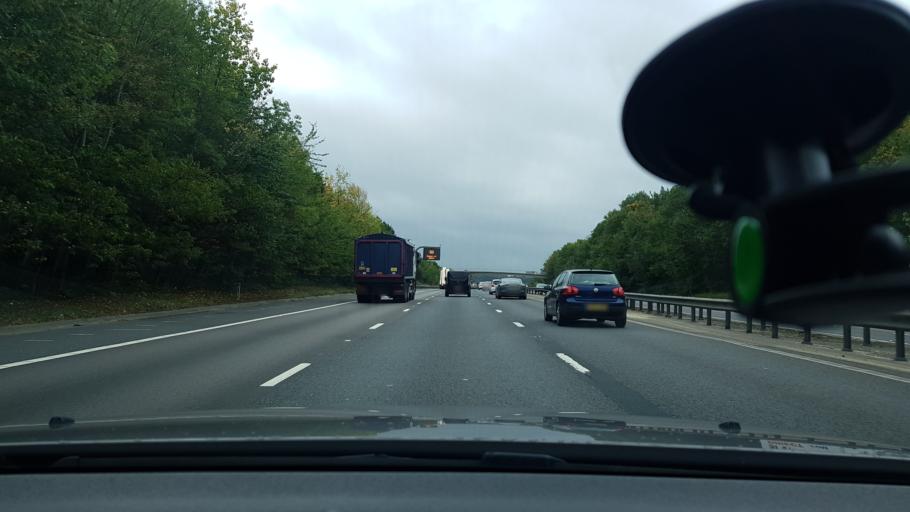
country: GB
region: England
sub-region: Hertfordshire
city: Sawbridgeworth
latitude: 51.8023
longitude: 0.1760
